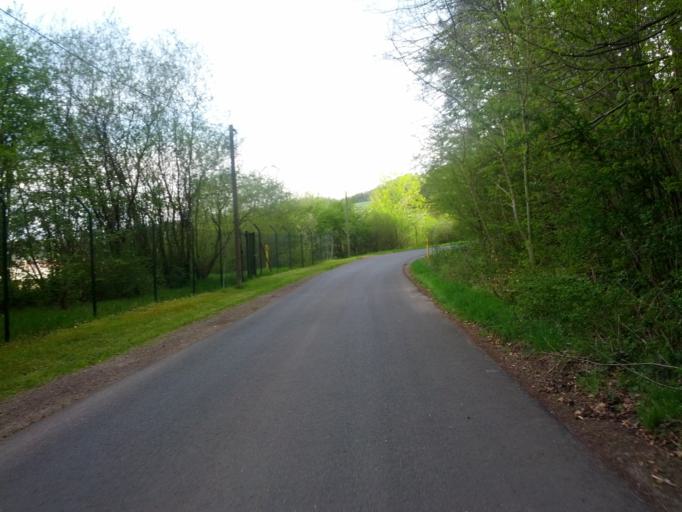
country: DE
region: Thuringia
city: Krauthausen
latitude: 51.0002
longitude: 10.2398
